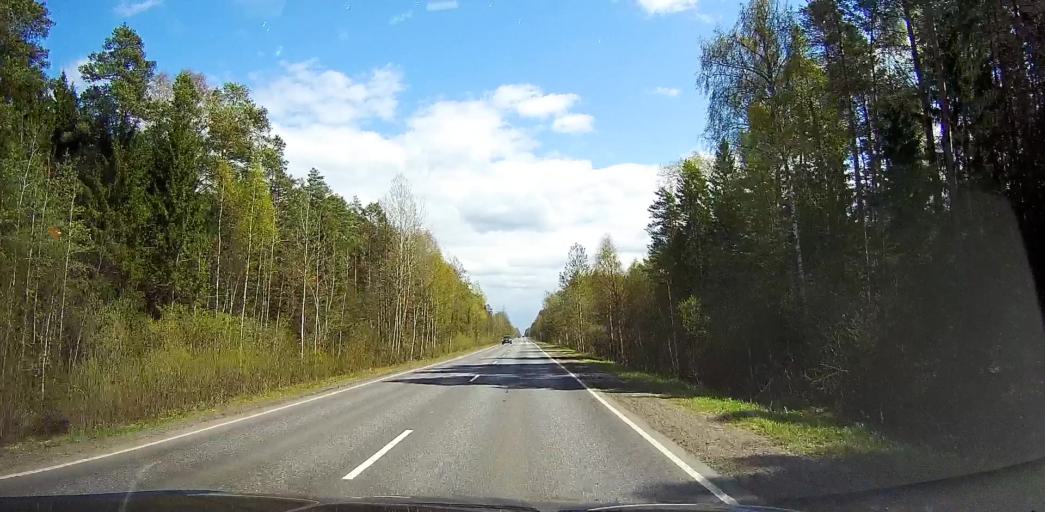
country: RU
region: Moskovskaya
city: Imeni Tsyurupy
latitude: 55.5515
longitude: 38.7234
